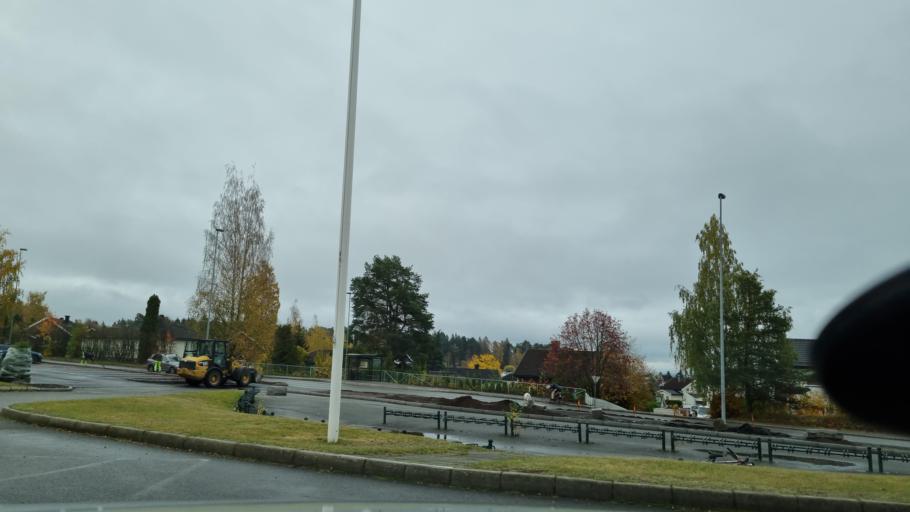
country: NO
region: Hedmark
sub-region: Hamar
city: Hamar
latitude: 60.8055
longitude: 11.0578
